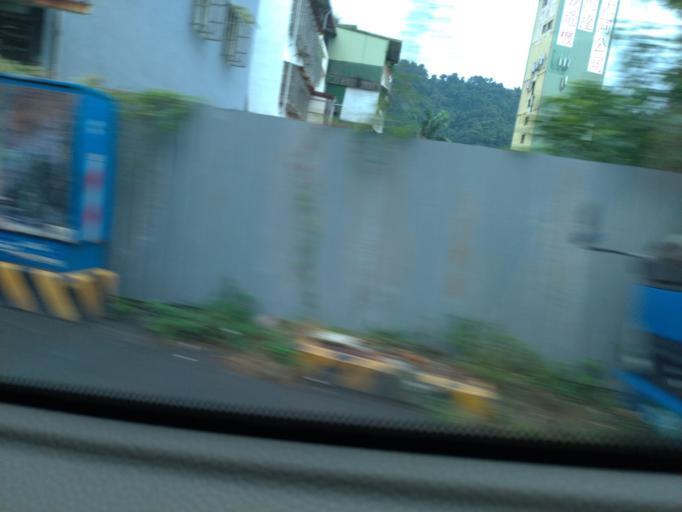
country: TW
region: Taipei
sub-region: Taipei
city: Banqiao
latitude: 24.9277
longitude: 121.4147
